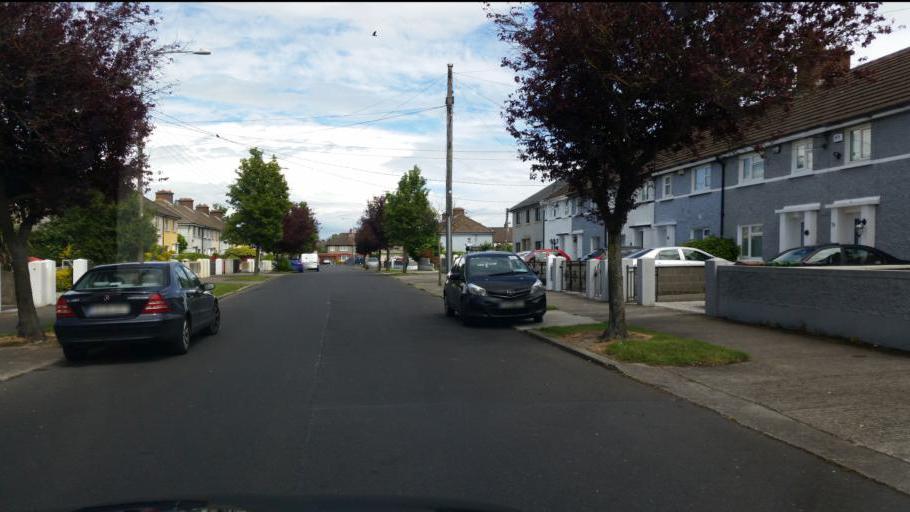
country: IE
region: Leinster
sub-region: Dublin City
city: Finglas
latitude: 53.3934
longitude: -6.2913
